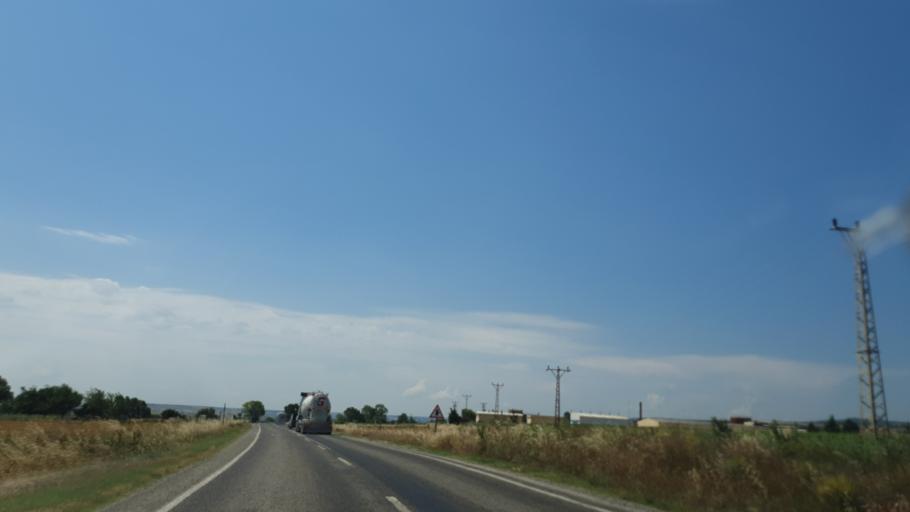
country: TR
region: Tekirdag
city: Saray
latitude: 41.5201
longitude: 27.8567
